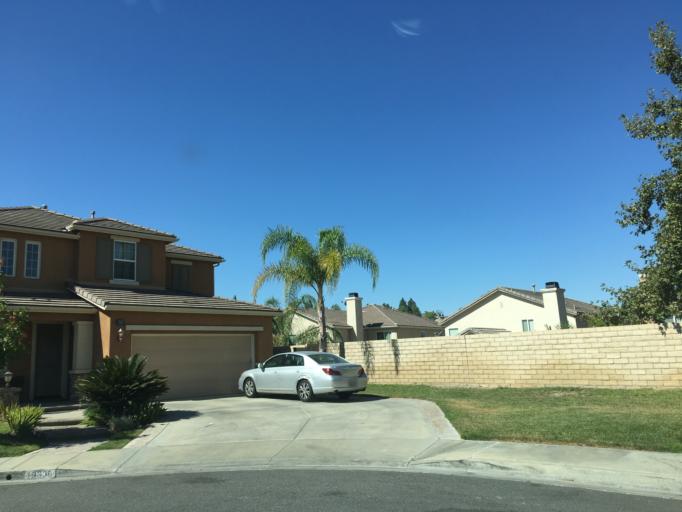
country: US
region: California
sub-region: Los Angeles County
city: Santa Clarita
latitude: 34.4440
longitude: -118.4797
